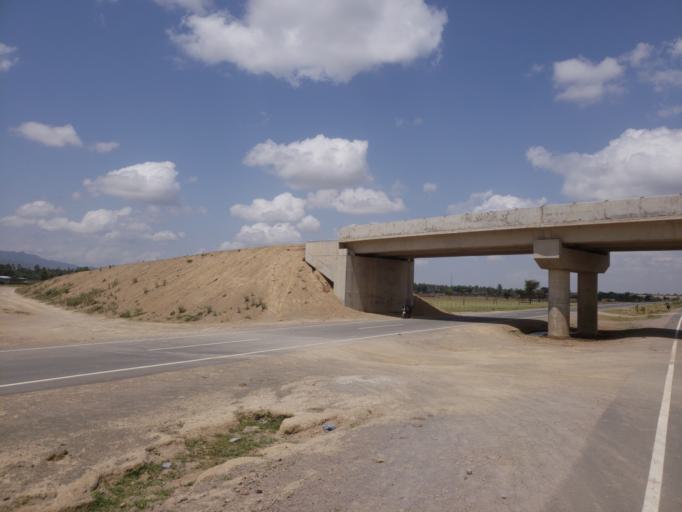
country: ET
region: Oromiya
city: Mojo
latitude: 8.3117
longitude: 38.9468
